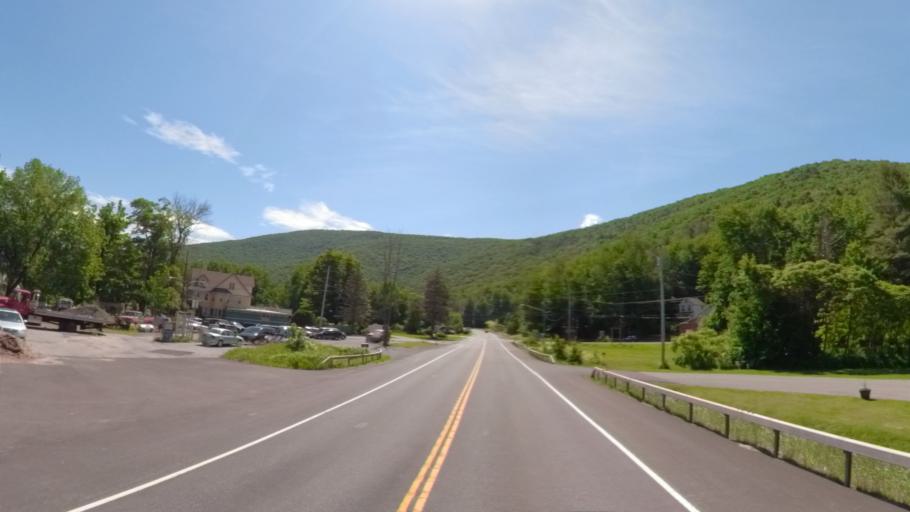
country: US
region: New York
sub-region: Ulster County
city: Shokan
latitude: 42.1033
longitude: -74.4446
